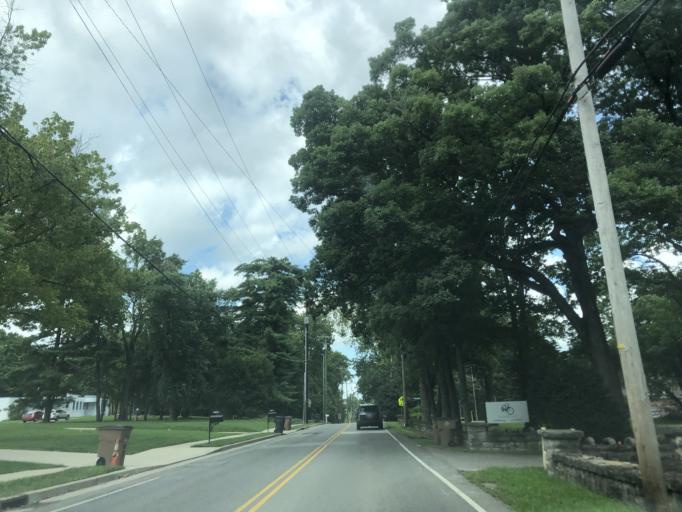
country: US
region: Tennessee
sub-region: Davidson County
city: Oak Hill
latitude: 36.0979
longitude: -86.8011
